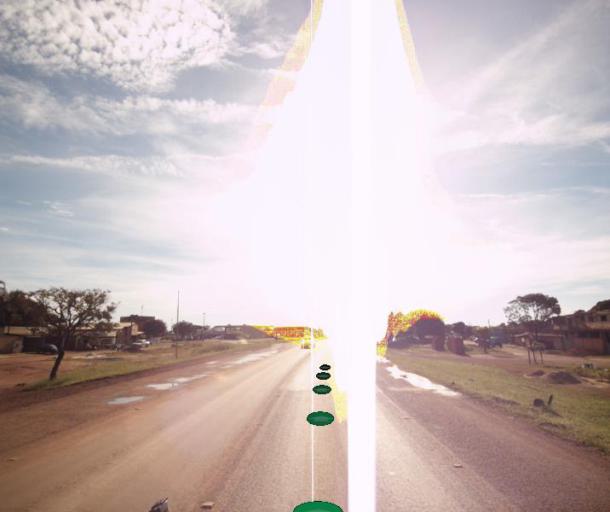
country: BR
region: Federal District
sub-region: Brasilia
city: Brasilia
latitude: -15.7372
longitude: -48.4067
